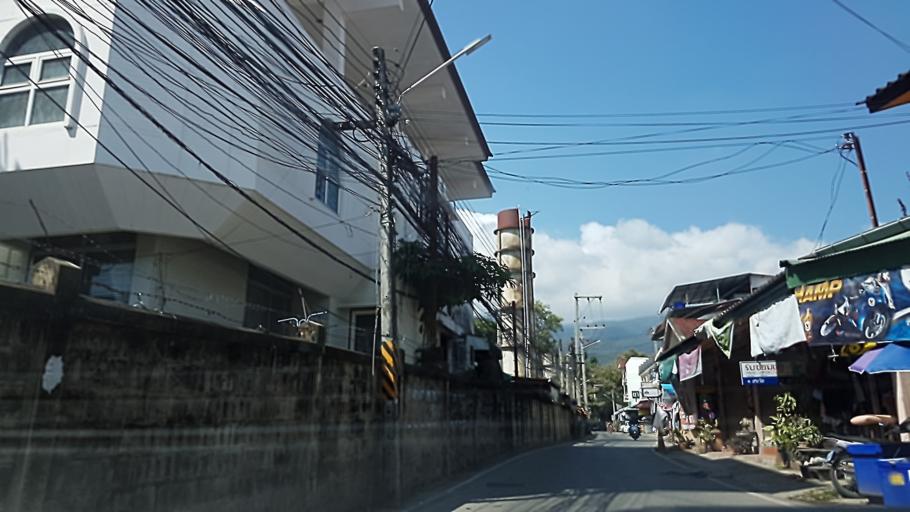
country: TH
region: Chiang Mai
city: Chiang Mai
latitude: 18.8092
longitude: 98.9605
